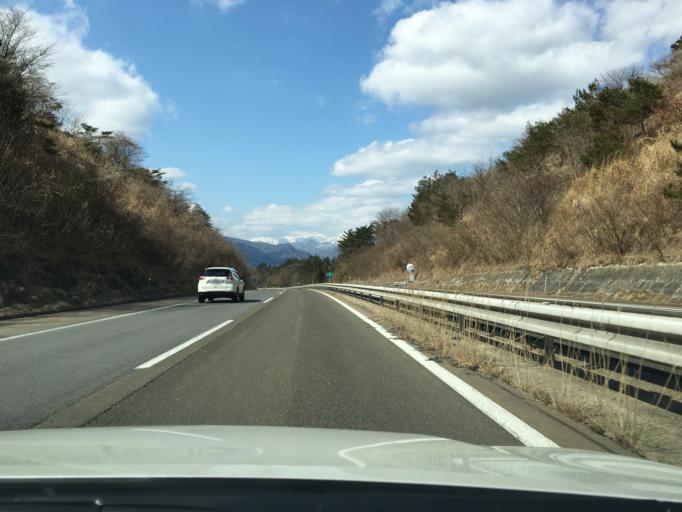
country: JP
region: Miyagi
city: Okawara
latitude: 38.1619
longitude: 140.6672
